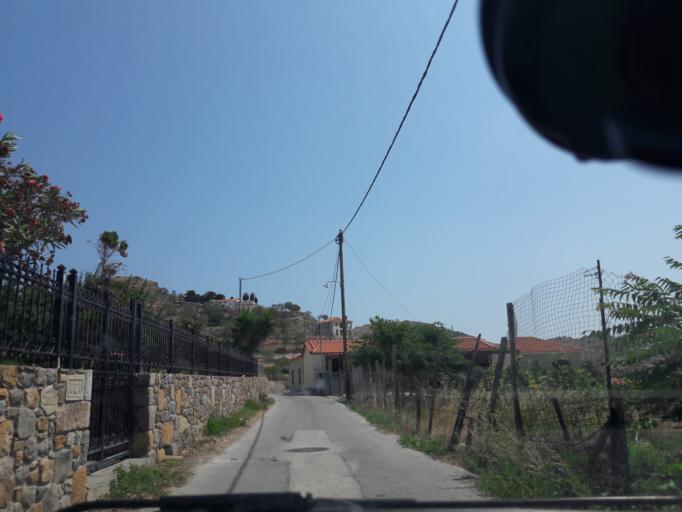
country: GR
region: North Aegean
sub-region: Nomos Lesvou
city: Myrina
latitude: 39.8531
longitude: 25.0869
